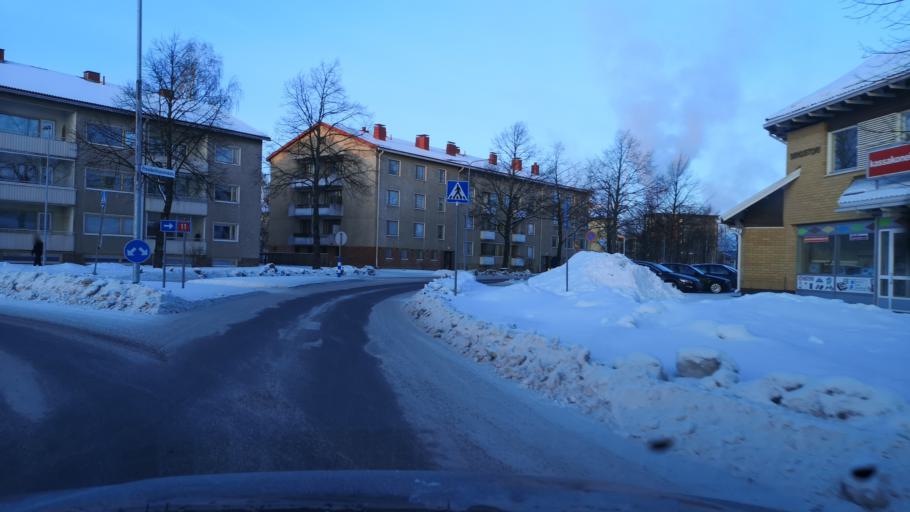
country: FI
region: Satakunta
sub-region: Pori
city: Pori
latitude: 61.4777
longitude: 21.8009
